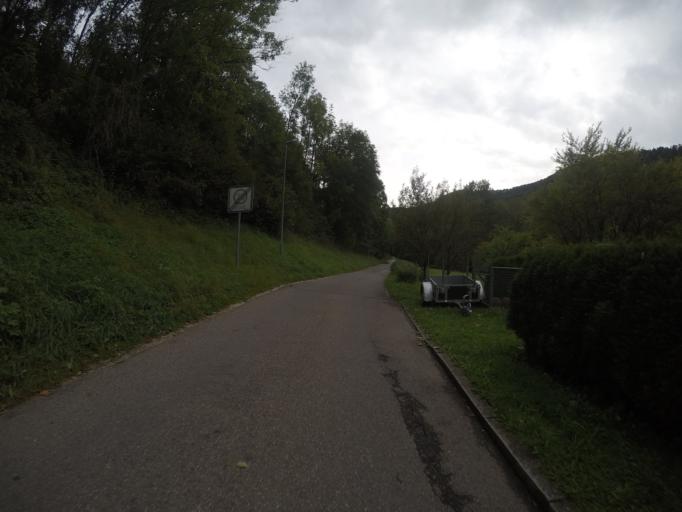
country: DE
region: Baden-Wuerttemberg
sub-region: Tuebingen Region
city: Pfullingen
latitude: 48.4227
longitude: 9.2567
